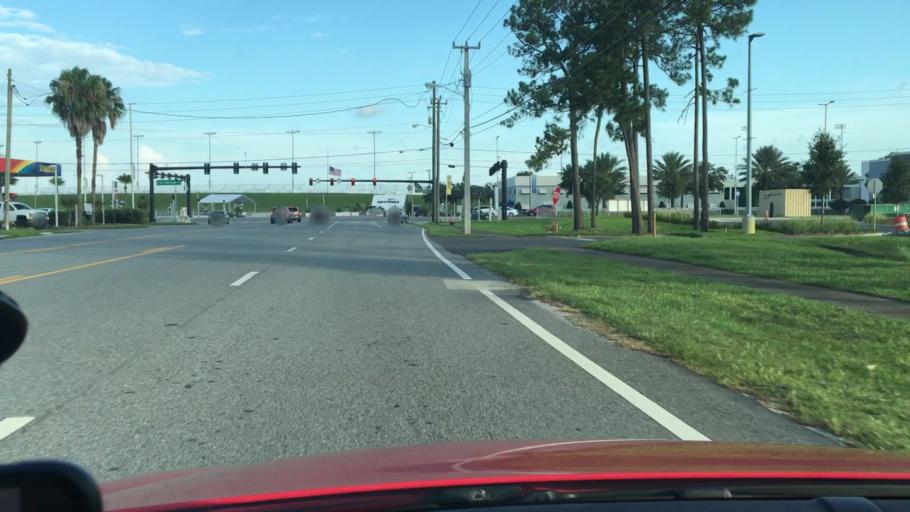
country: US
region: Florida
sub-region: Volusia County
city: Daytona Beach
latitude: 29.1940
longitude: -81.0675
